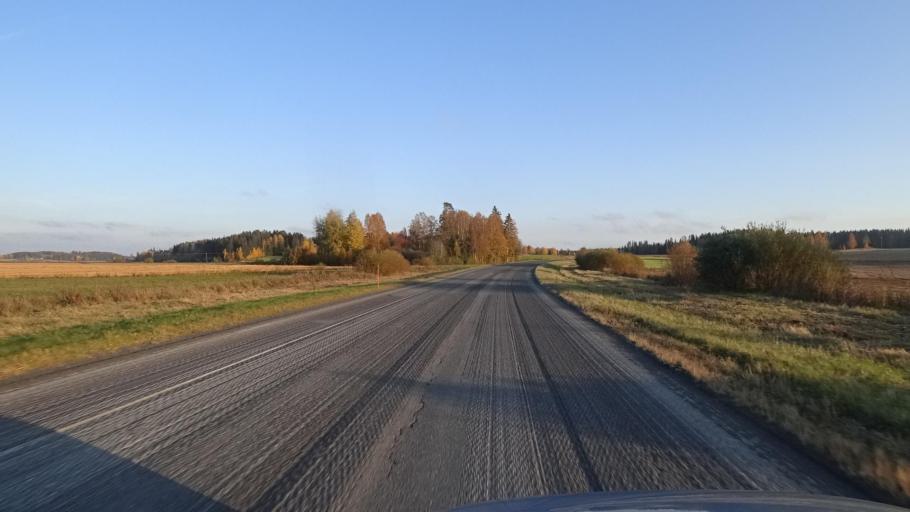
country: FI
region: Haeme
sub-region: Forssa
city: Ypaejae
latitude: 60.7844
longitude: 23.3039
